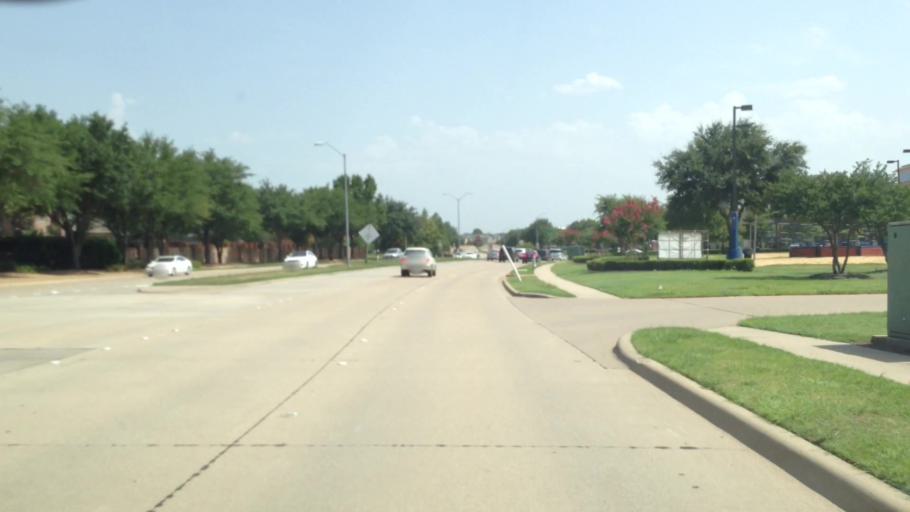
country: US
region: Texas
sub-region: Dallas County
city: Addison
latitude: 33.0364
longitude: -96.8273
